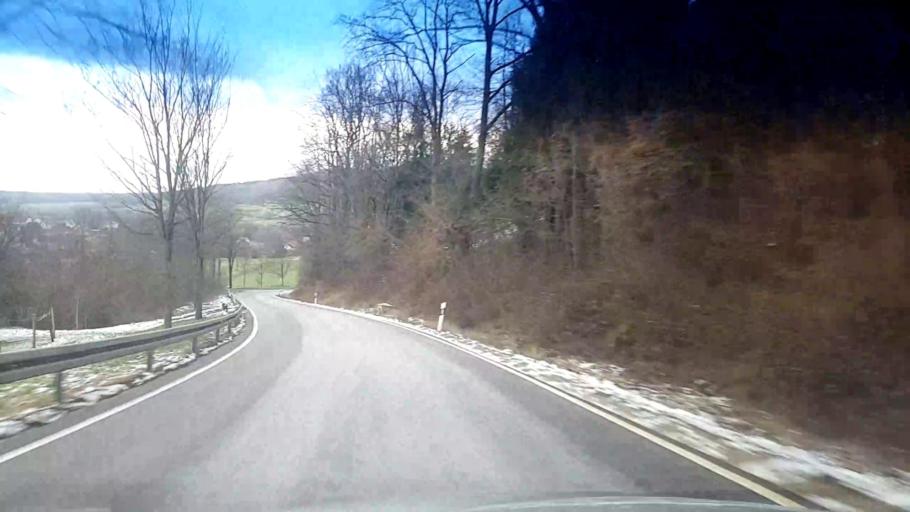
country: DE
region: Bavaria
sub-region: Upper Franconia
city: Litzendorf
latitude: 49.8706
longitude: 11.0743
